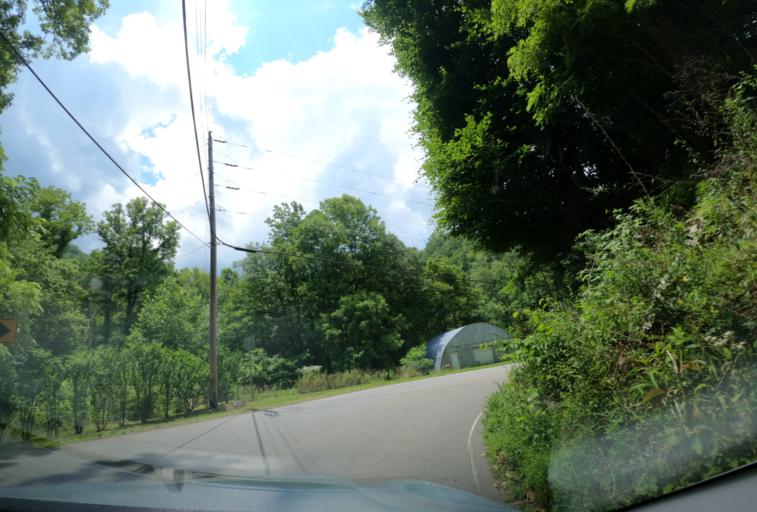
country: US
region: North Carolina
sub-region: Haywood County
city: Waynesville
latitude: 35.4226
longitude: -82.9127
